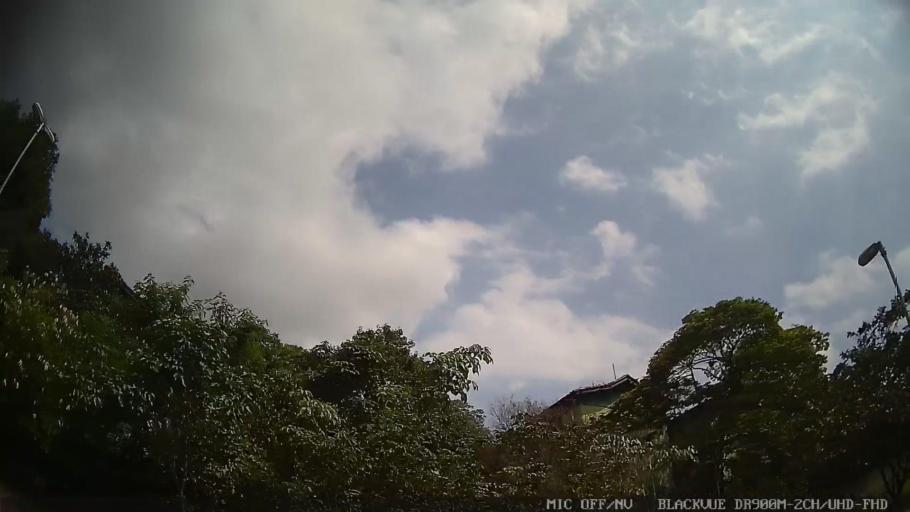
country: BR
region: Sao Paulo
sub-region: Taboao Da Serra
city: Taboao da Serra
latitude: -23.6640
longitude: -46.7301
